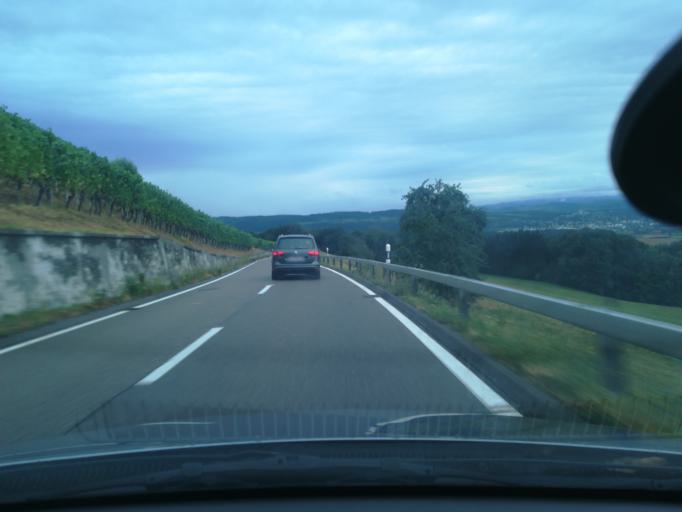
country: CH
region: Thurgau
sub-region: Frauenfeld District
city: Huttwilen
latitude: 47.6096
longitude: 8.8920
